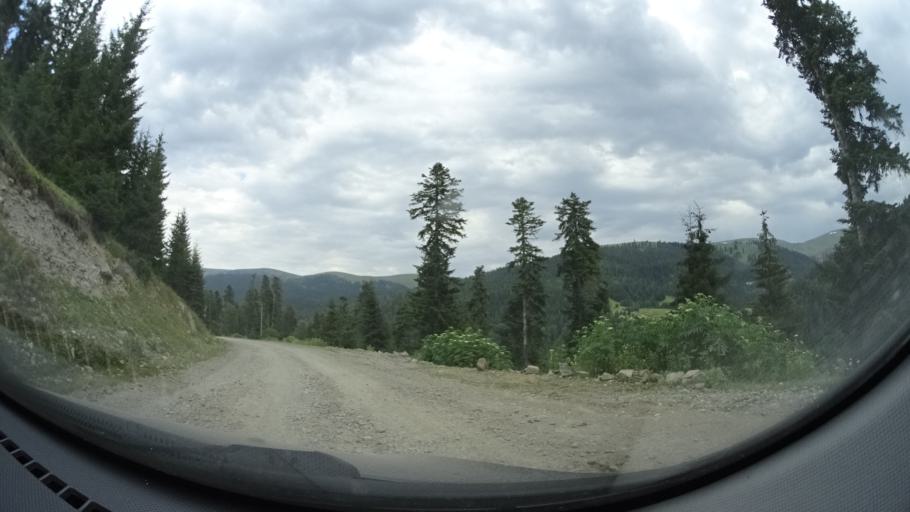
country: GE
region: Samtskhe-Javakheti
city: Adigeni
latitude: 41.6308
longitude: 42.5689
